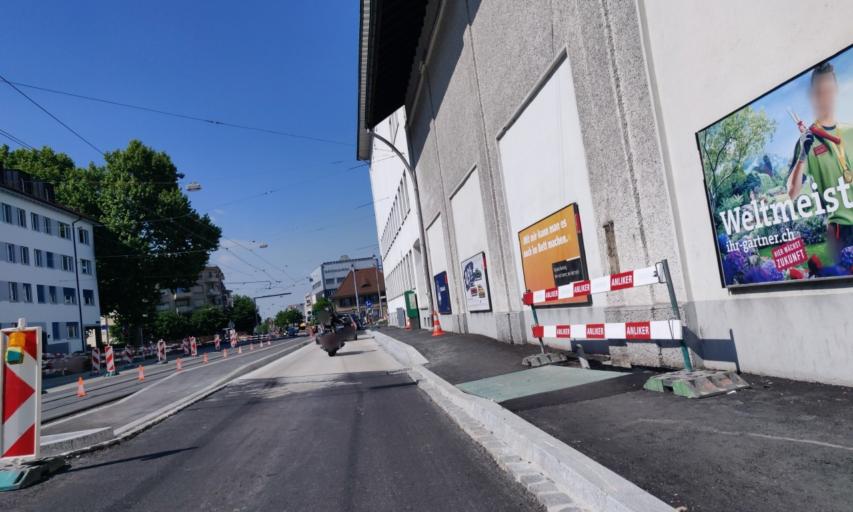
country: CH
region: Basel-Landschaft
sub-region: Bezirk Arlesheim
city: Munchenstein
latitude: 47.5360
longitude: 7.6045
